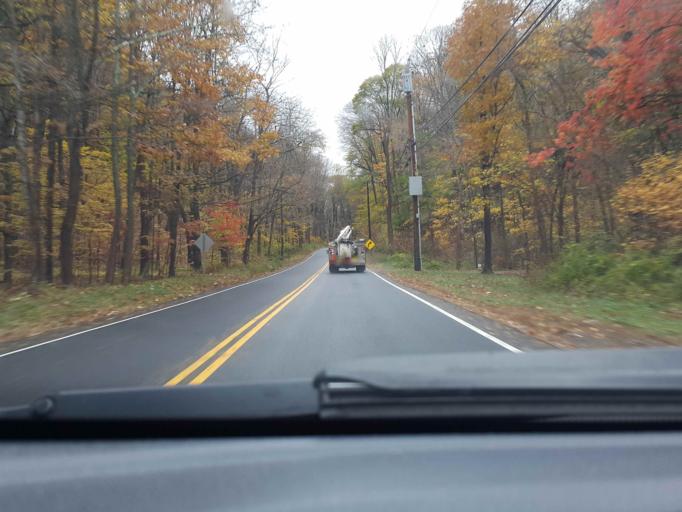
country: US
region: Connecticut
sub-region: Middlesex County
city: Durham
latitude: 41.4077
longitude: -72.6963
